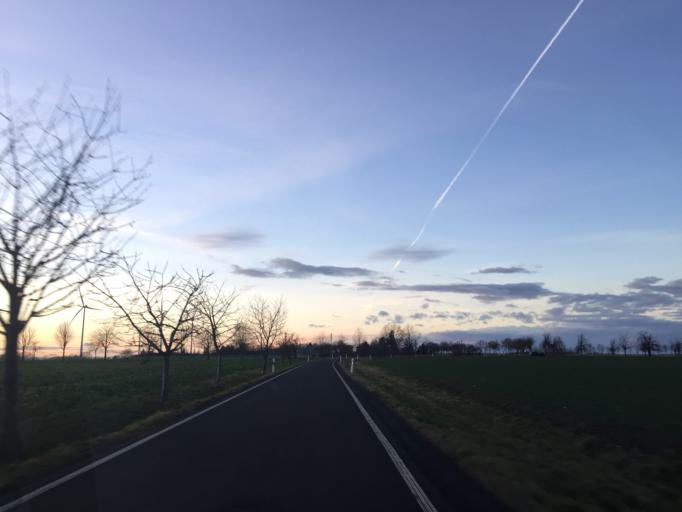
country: DE
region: Thuringia
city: Schmolln
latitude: 50.9020
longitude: 12.3345
